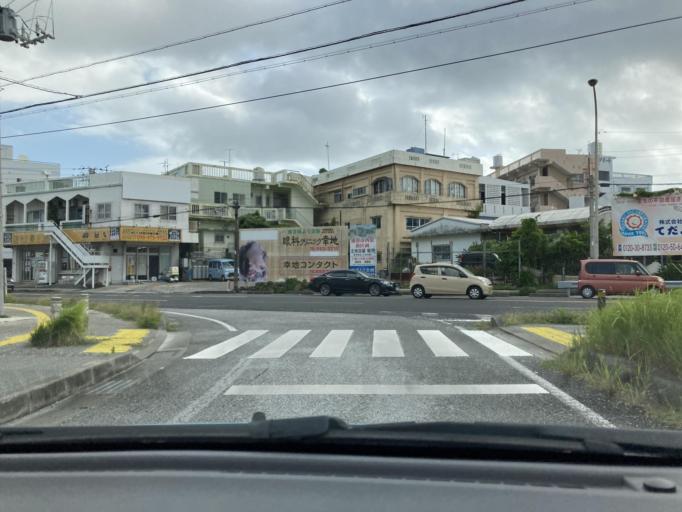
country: JP
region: Okinawa
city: Ginowan
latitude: 26.2540
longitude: 127.7390
